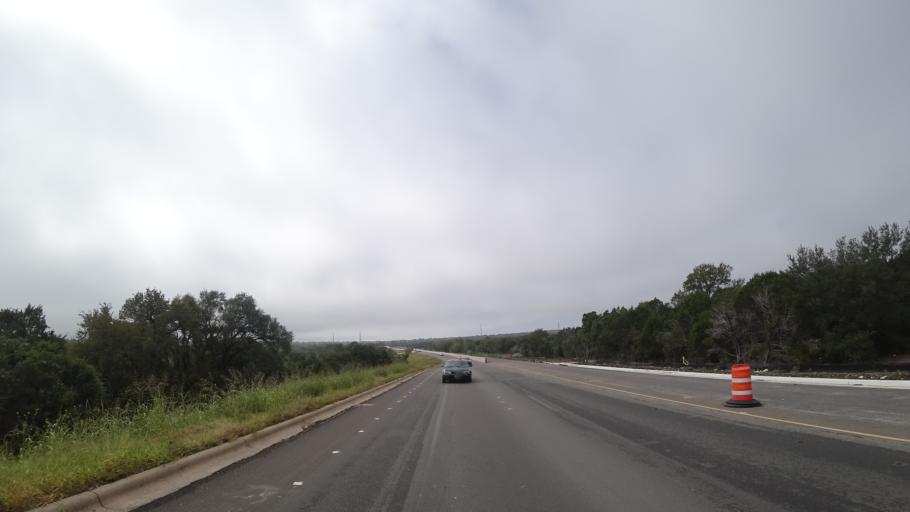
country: US
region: Texas
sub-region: Travis County
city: Shady Hollow
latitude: 30.1792
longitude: -97.8822
